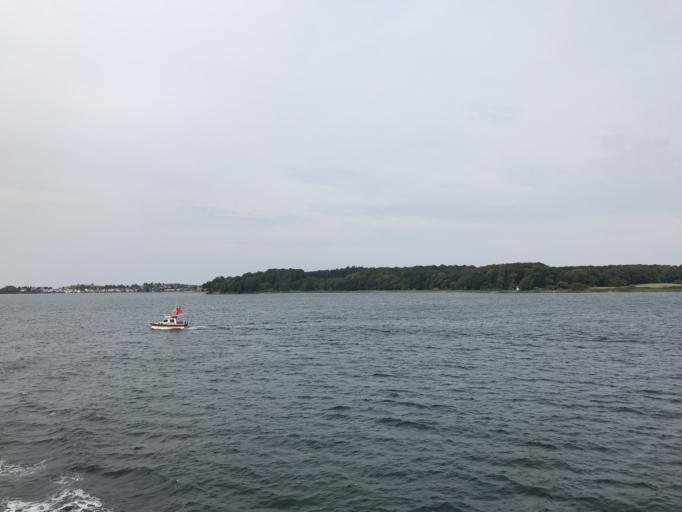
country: DK
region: South Denmark
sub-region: Faaborg-Midtfyn Kommune
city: Faaborg
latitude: 55.0744
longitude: 10.2374
